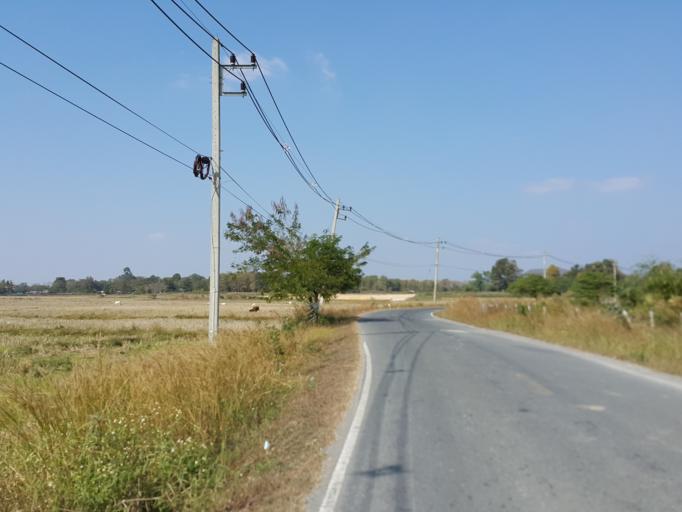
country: TH
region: Chiang Mai
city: Mae On
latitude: 18.8064
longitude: 99.1729
